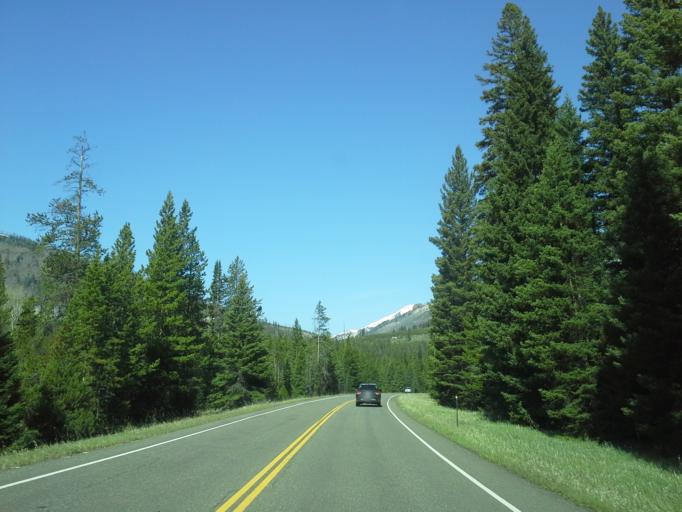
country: US
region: Montana
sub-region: Carbon County
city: Red Lodge
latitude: 44.9576
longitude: -109.8078
